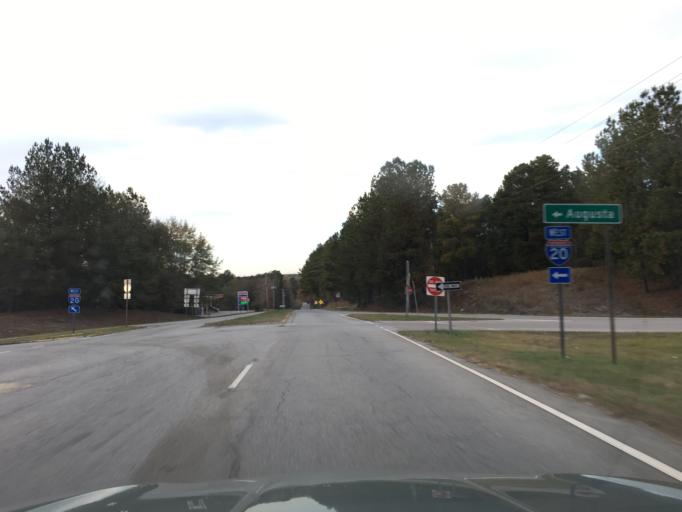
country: US
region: South Carolina
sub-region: Lexington County
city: Leesville
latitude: 33.8172
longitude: -81.4527
